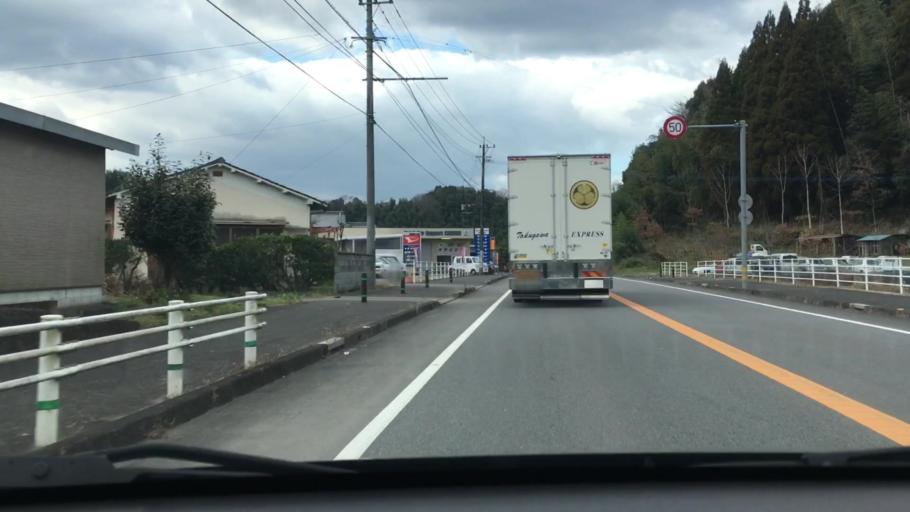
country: JP
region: Oita
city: Usuki
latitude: 33.0655
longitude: 131.6583
